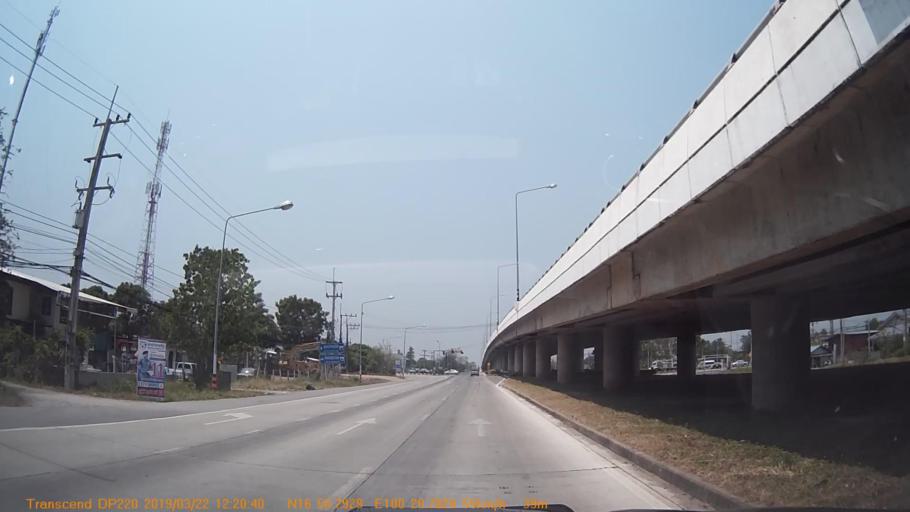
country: TH
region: Phitsanulok
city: Wang Thong
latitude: 16.8466
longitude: 100.3461
